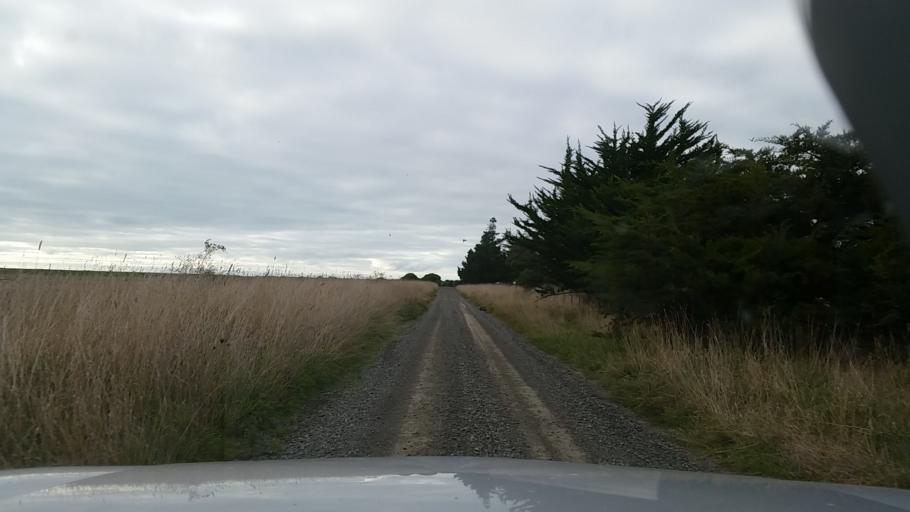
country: NZ
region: Marlborough
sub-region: Marlborough District
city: Blenheim
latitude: -41.5128
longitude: 174.0428
